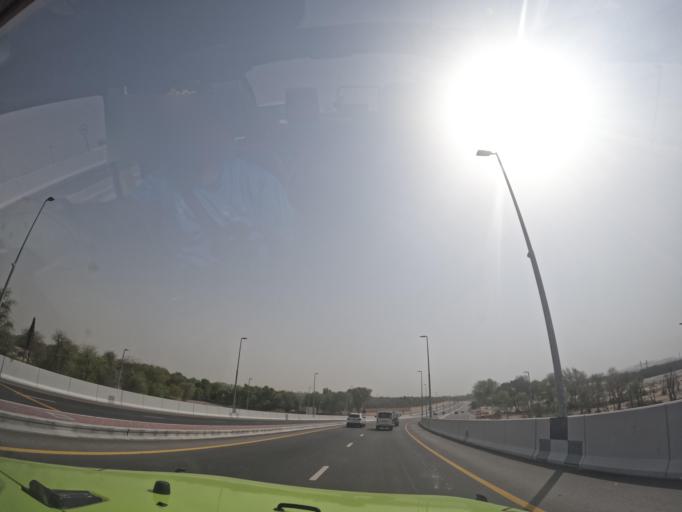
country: AE
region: Dubai
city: Dubai
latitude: 25.1528
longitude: 55.3350
